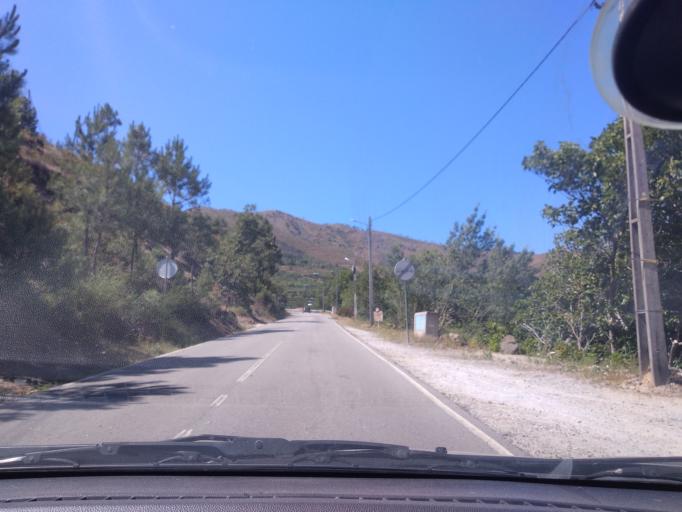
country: PT
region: Castelo Branco
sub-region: Concelho do Fundao
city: Fundao
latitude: 40.1241
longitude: -7.4884
